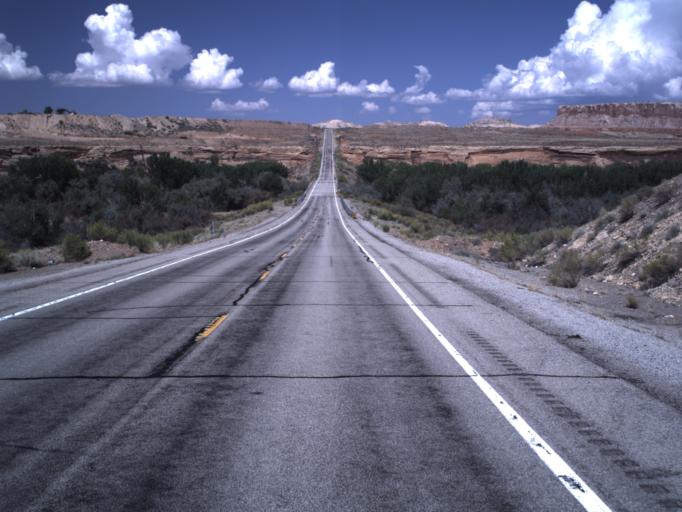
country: US
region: Utah
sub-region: San Juan County
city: Blanding
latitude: 37.2553
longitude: -109.6161
